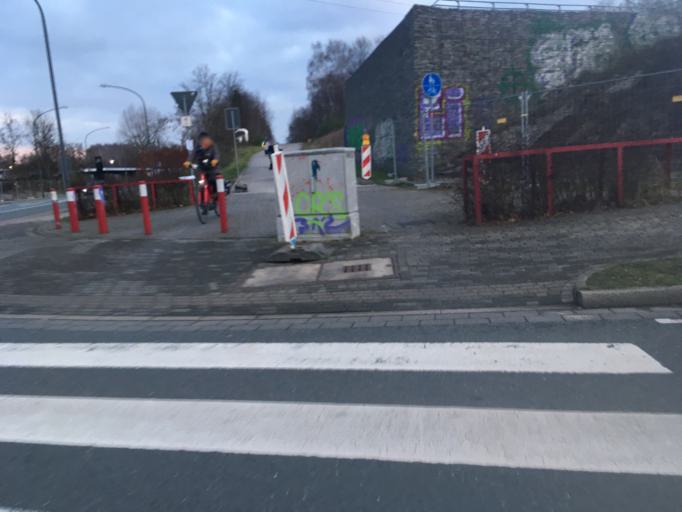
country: DE
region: North Rhine-Westphalia
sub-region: Regierungsbezirk Dusseldorf
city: Essen
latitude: 51.4657
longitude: 6.9875
